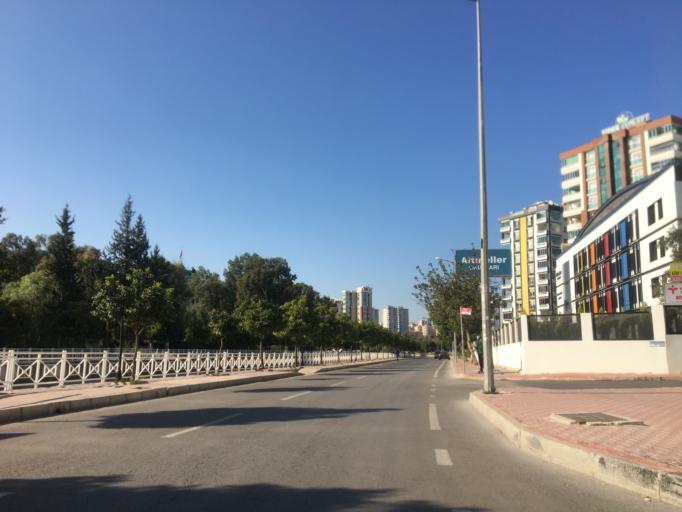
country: TR
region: Adana
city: Seyhan
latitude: 37.0272
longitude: 35.2729
